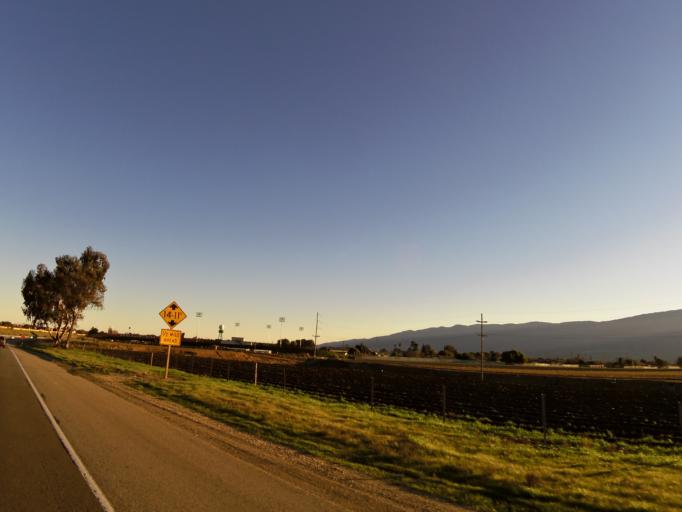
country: US
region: California
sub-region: Monterey County
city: Gonzales
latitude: 36.5196
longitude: -121.4441
